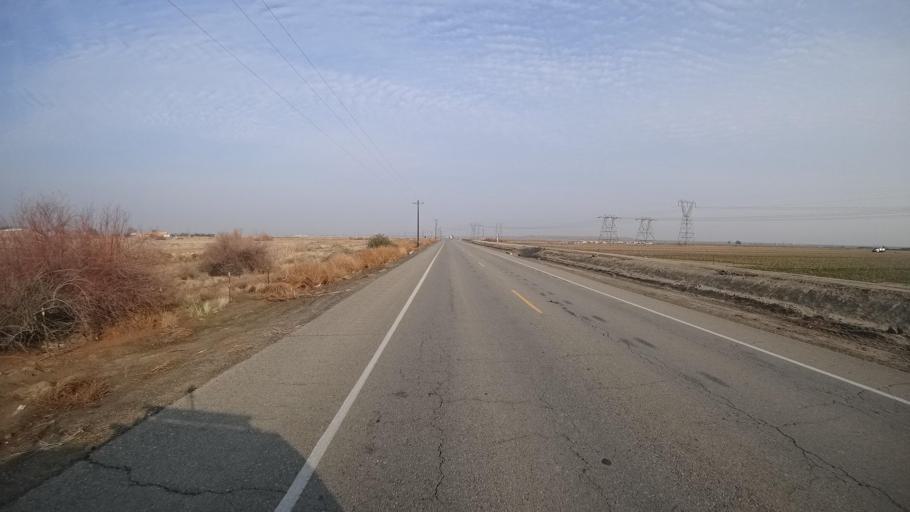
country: US
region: California
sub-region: Kern County
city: Weedpatch
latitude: 35.1747
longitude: -118.9151
